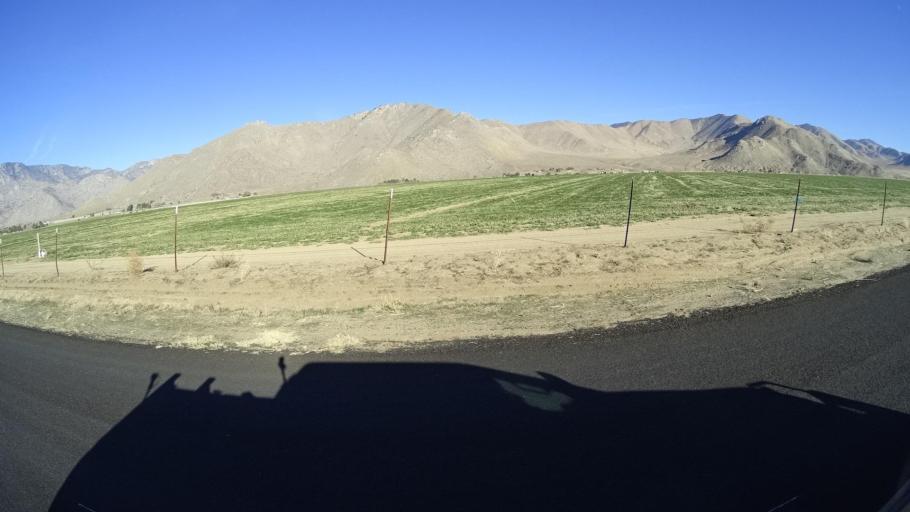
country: US
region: California
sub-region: Kern County
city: Weldon
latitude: 35.6374
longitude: -118.2683
